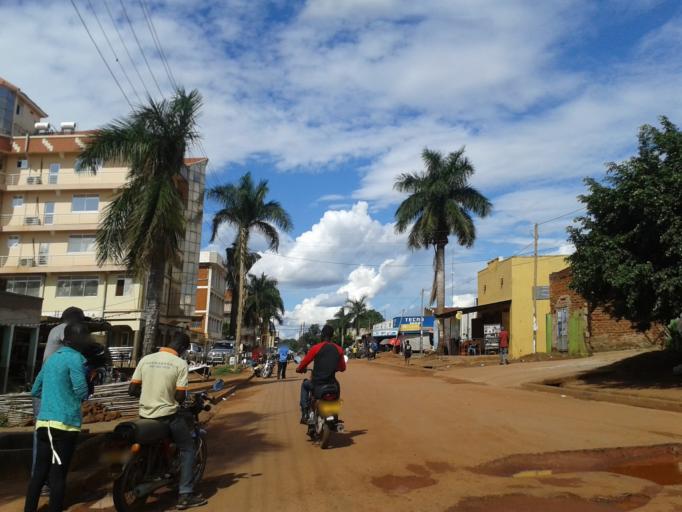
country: UG
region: Northern Region
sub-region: Gulu District
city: Gulu
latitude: 2.7736
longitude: 32.2984
